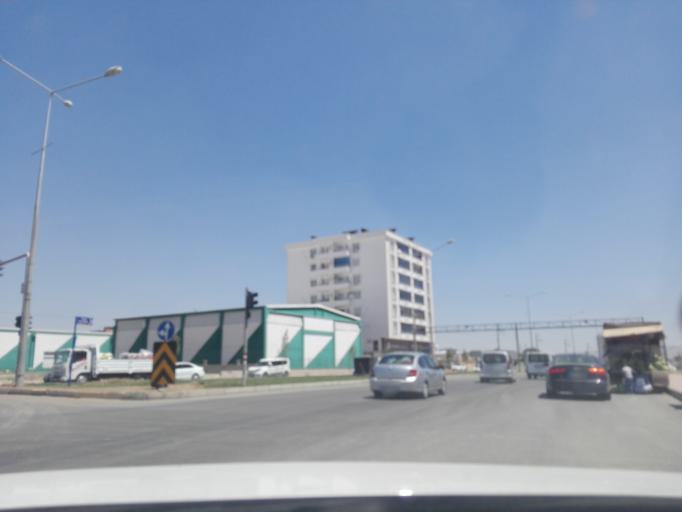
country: TR
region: Batman
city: Aydinkonak
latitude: 37.8907
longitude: 41.1530
